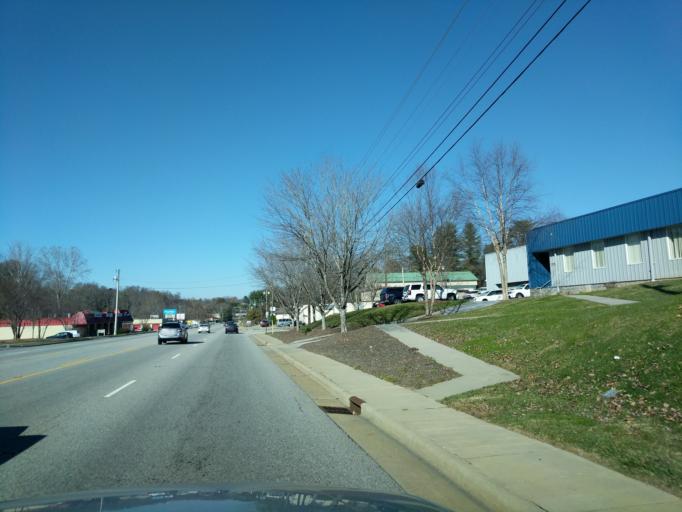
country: US
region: North Carolina
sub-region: Buncombe County
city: Biltmore Forest
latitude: 35.5399
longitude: -82.5204
